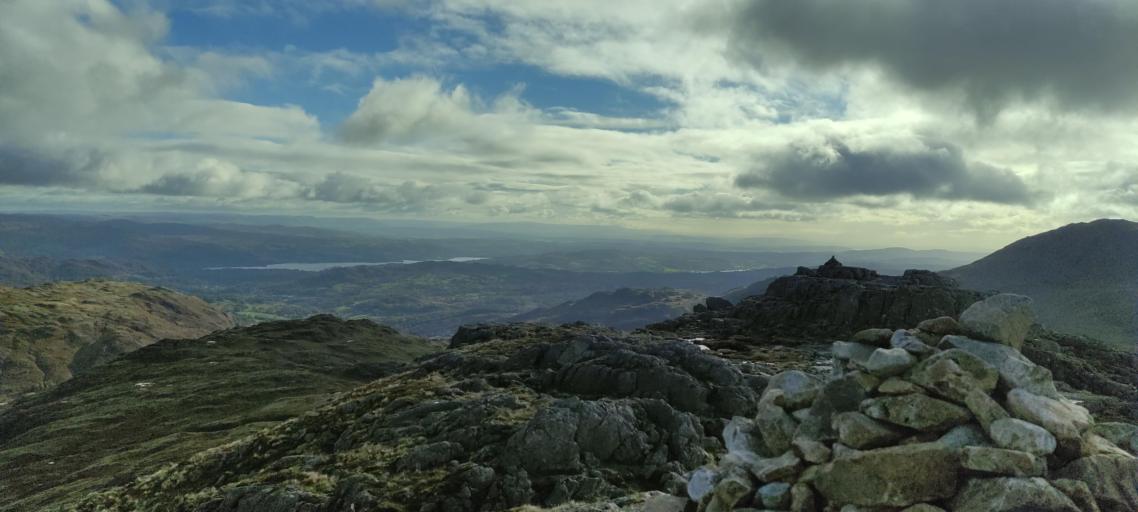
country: GB
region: England
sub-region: Cumbria
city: Ambleside
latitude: 54.4282
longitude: -3.1250
